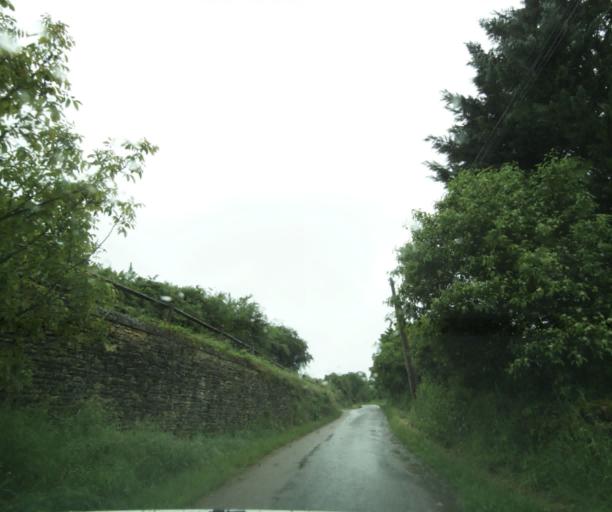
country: FR
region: Bourgogne
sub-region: Departement de Saone-et-Loire
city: Charolles
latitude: 46.4009
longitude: 4.2674
